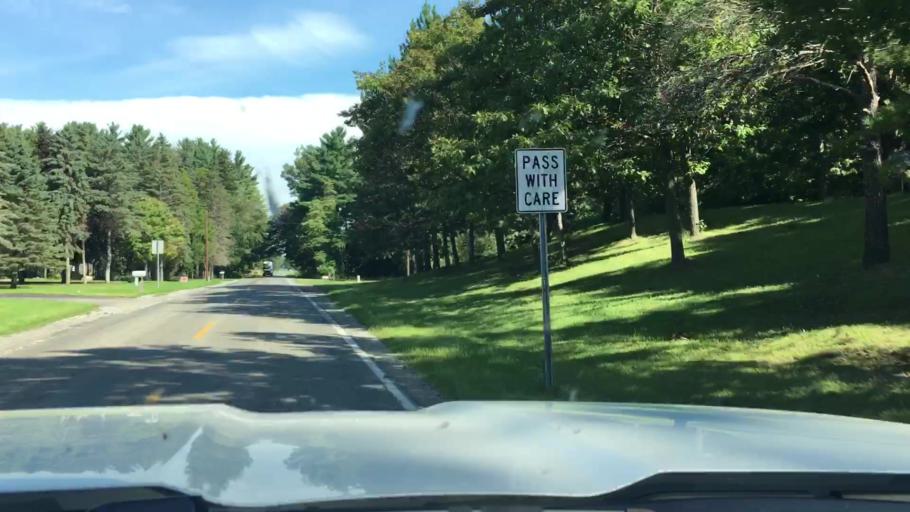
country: US
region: Michigan
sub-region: Saginaw County
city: Hemlock
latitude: 43.4620
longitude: -84.2303
